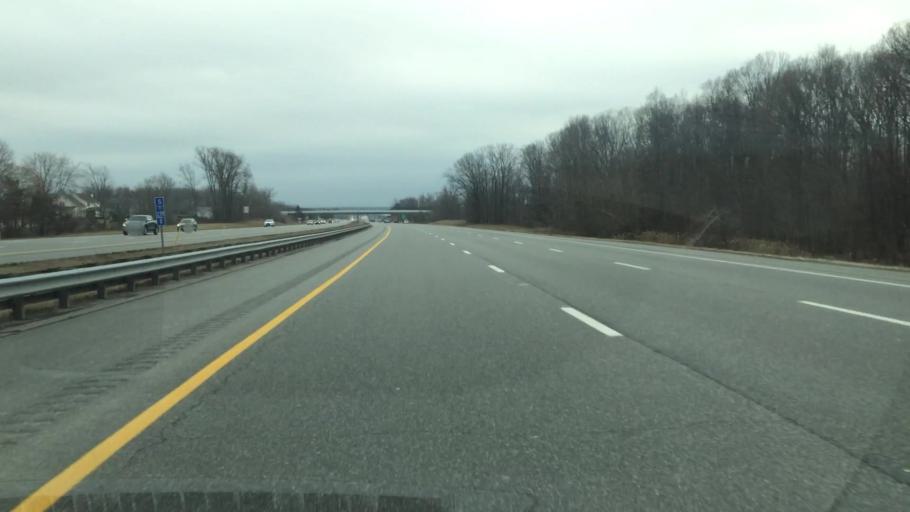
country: US
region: Ohio
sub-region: Cuyahoga County
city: Strongsville
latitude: 41.2807
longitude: -81.8075
